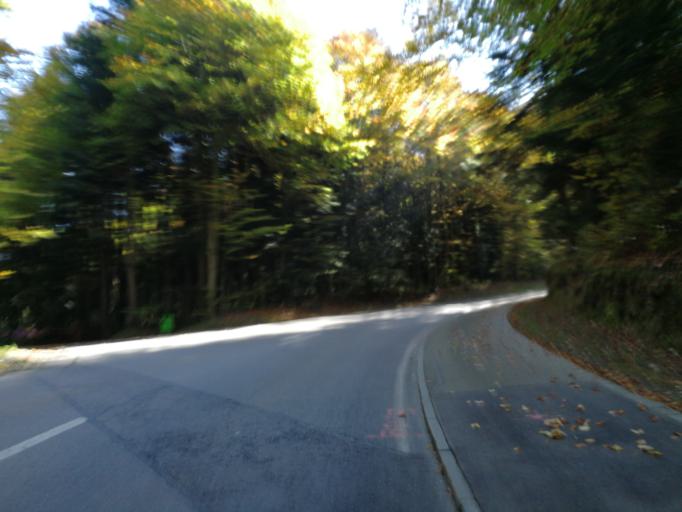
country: CH
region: Schwyz
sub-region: Bezirk March
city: Altendorf
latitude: 47.1991
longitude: 8.7989
